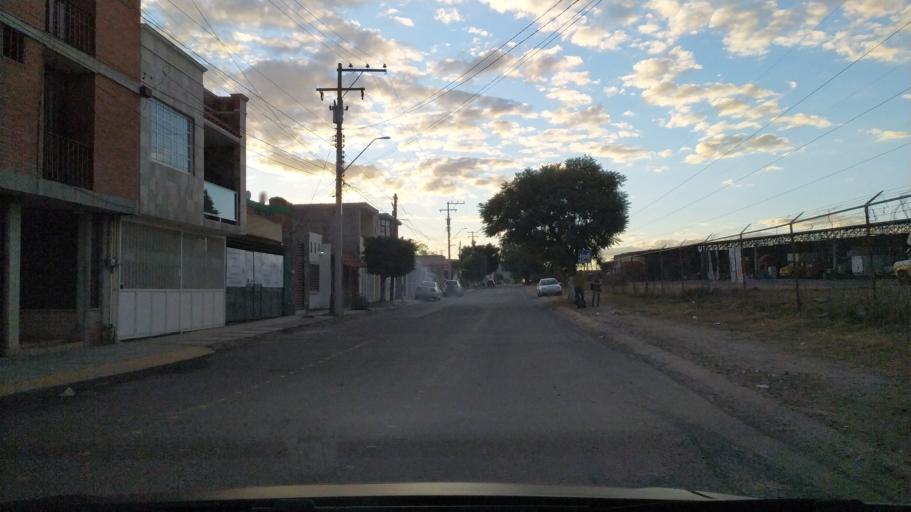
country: MX
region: Guanajuato
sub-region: San Francisco del Rincon
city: Estacion de San Francisco
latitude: 21.0389
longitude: -101.8446
